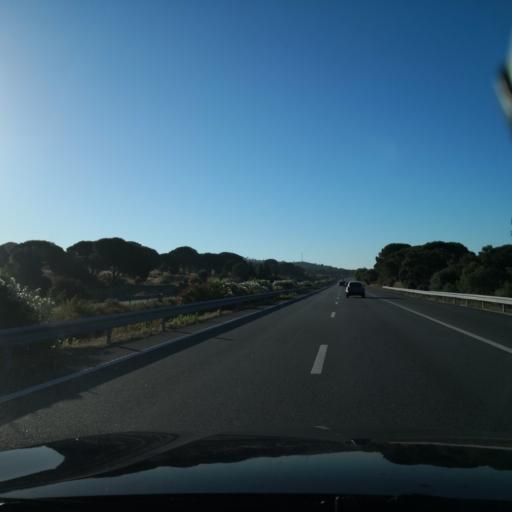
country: PT
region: Setubal
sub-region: Alcacer do Sal
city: Alcacer do Sal
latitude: 38.4867
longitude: -8.5532
